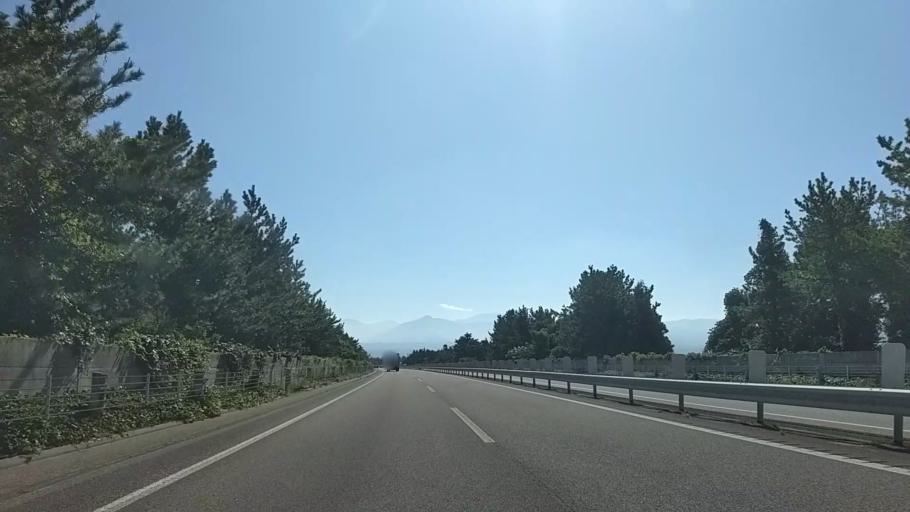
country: JP
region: Toyama
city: Toyama-shi
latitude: 36.6498
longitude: 137.2160
